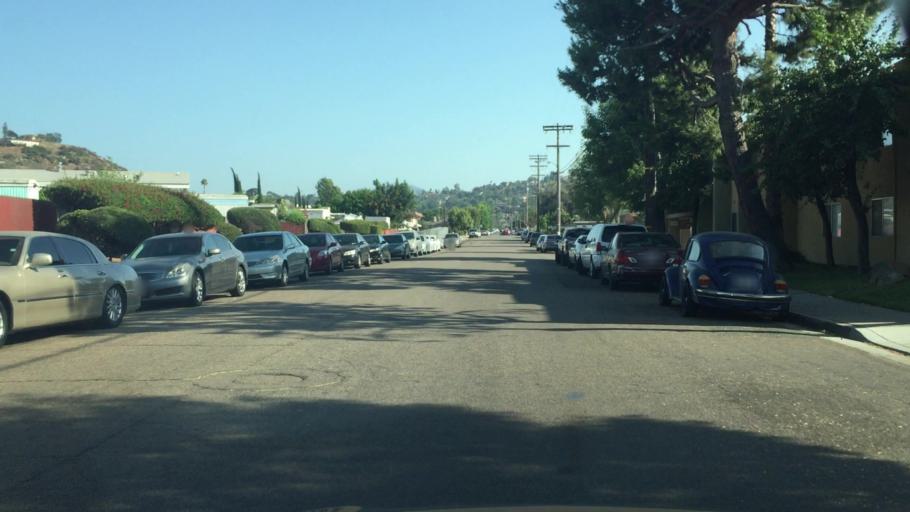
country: US
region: California
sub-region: San Diego County
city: El Cajon
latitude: 32.7905
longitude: -116.9482
